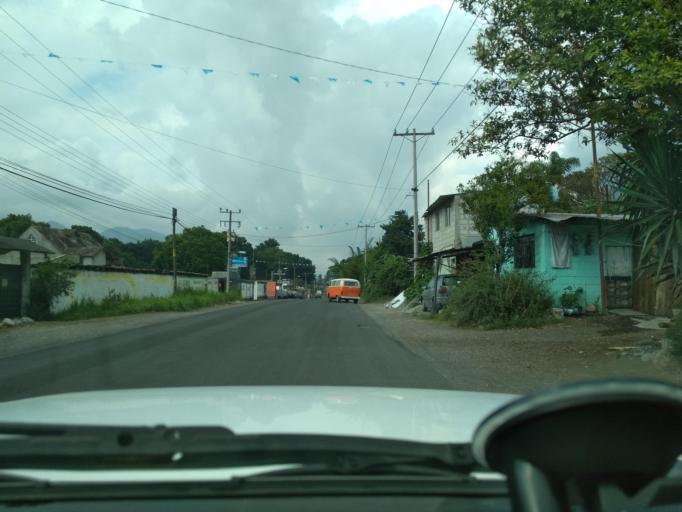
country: MX
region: Veracruz
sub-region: Nogales
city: Taza de Agua Ojo Zarco
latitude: 18.7865
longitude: -97.2000
